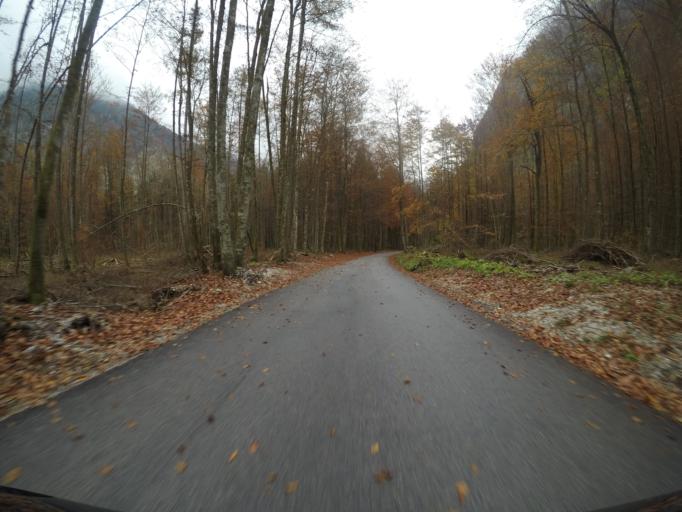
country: SI
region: Jesenice
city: Hrusica
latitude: 46.4288
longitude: 13.9499
